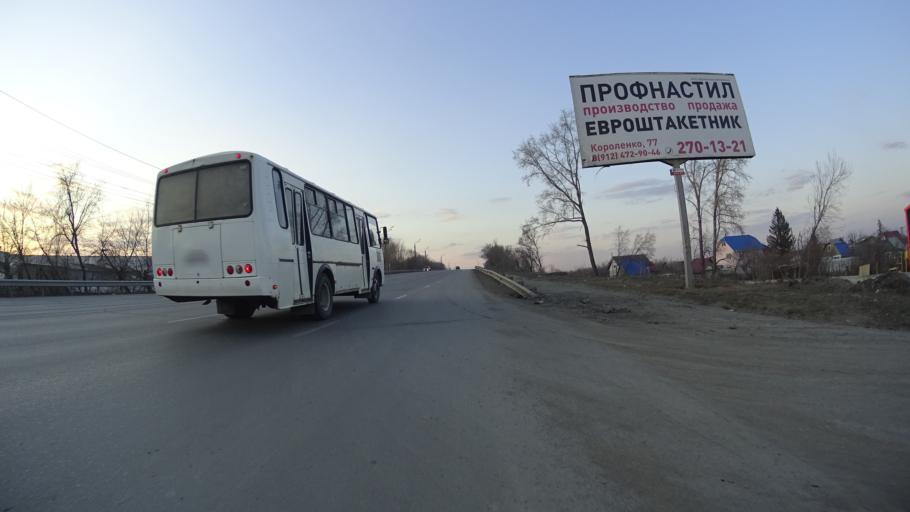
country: RU
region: Chelyabinsk
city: Novosineglazovskiy
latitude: 55.0989
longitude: 61.3879
